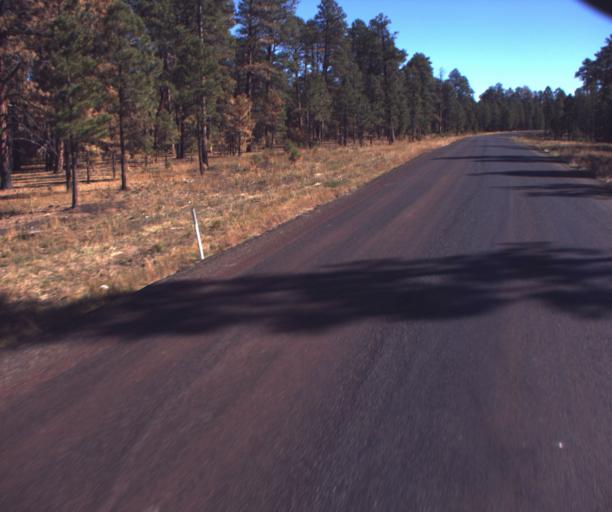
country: US
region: Arizona
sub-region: Coconino County
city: Fredonia
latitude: 36.7489
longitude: -112.2656
